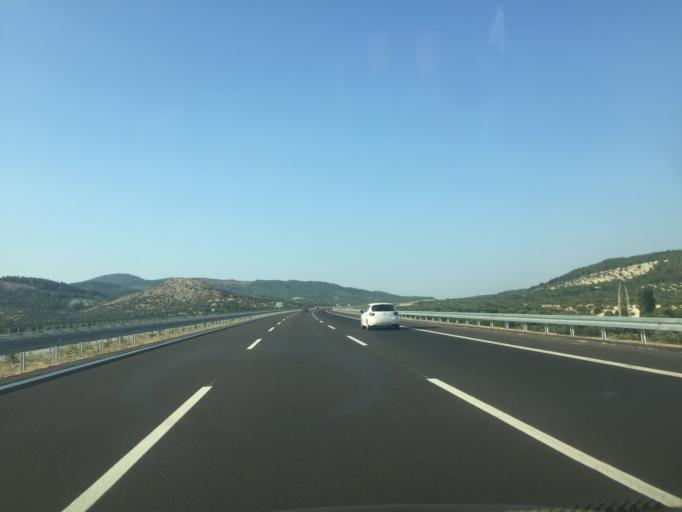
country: TR
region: Manisa
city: Zeytinliova
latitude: 38.9834
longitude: 27.7315
